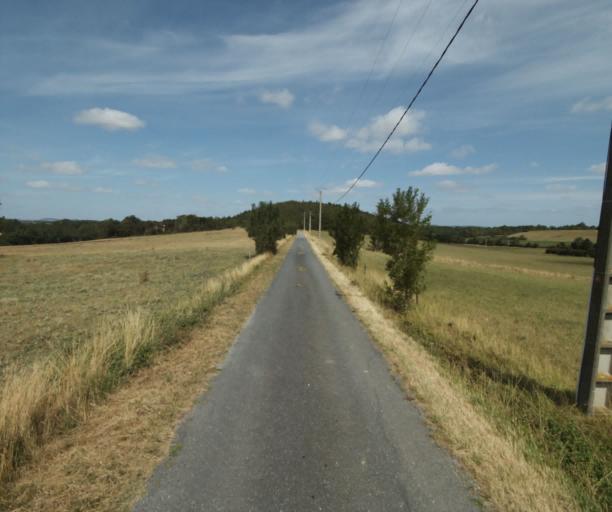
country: FR
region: Midi-Pyrenees
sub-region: Departement du Tarn
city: Dourgne
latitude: 43.4739
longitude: 2.1147
